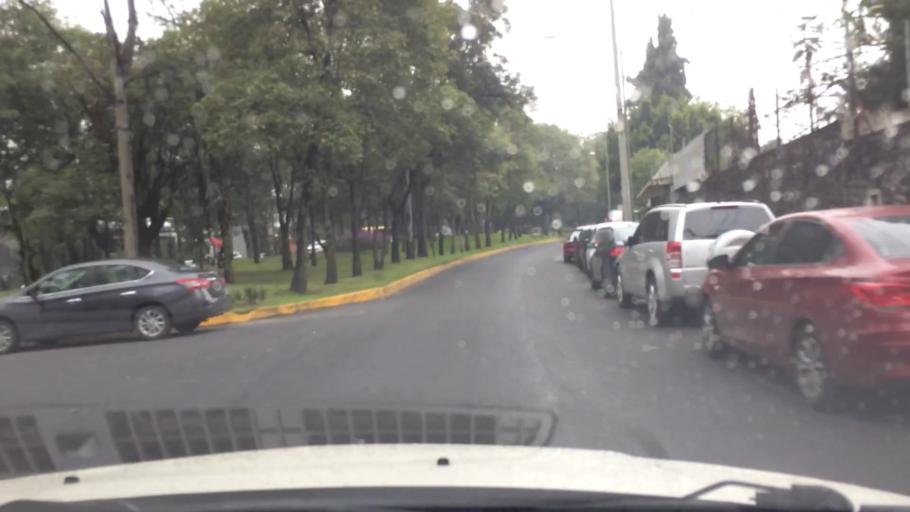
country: MX
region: Mexico City
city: Magdalena Contreras
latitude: 19.3087
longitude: -99.2082
